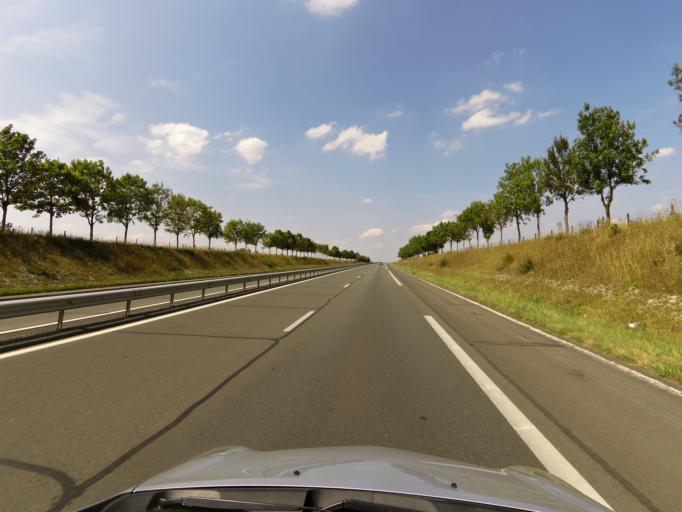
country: FR
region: Picardie
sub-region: Departement de l'Aisne
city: Saint-Erme-Outre-et-Ramecourt
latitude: 49.4857
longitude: 3.9022
